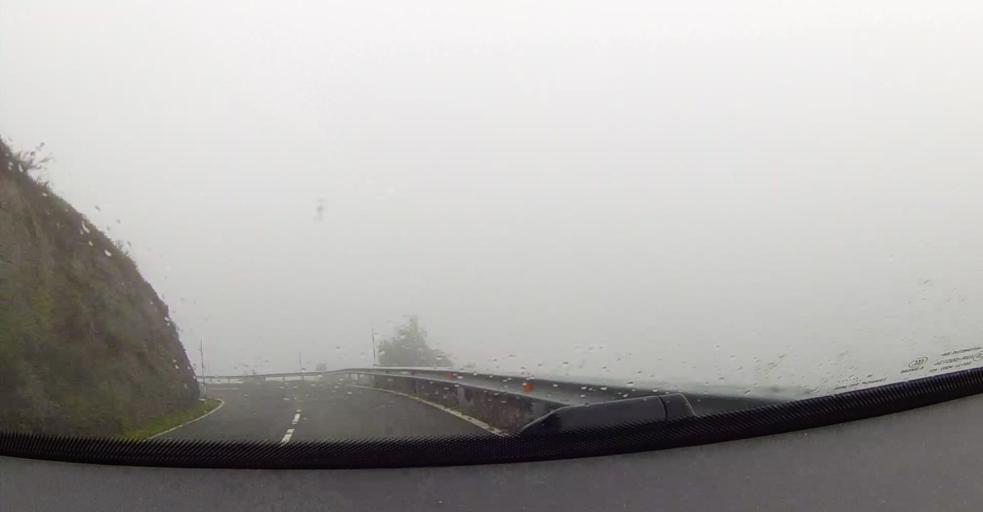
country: ES
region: Cantabria
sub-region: Provincia de Cantabria
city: Camaleno
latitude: 43.0767
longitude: -4.7287
